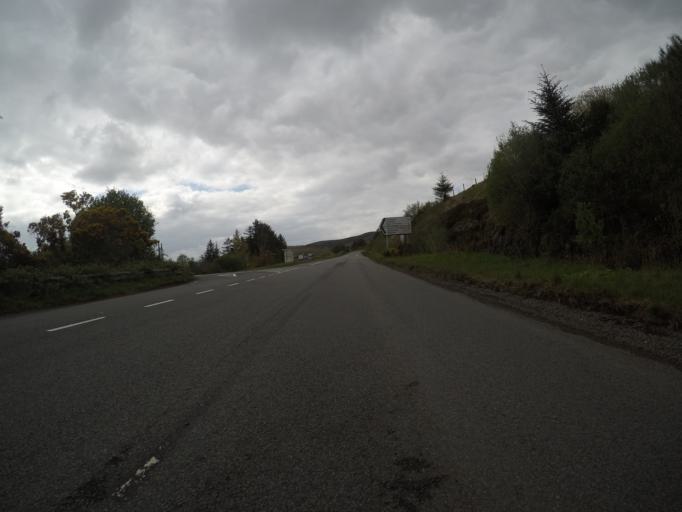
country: GB
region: Scotland
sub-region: Highland
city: Isle of Skye
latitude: 57.2988
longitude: -6.2925
